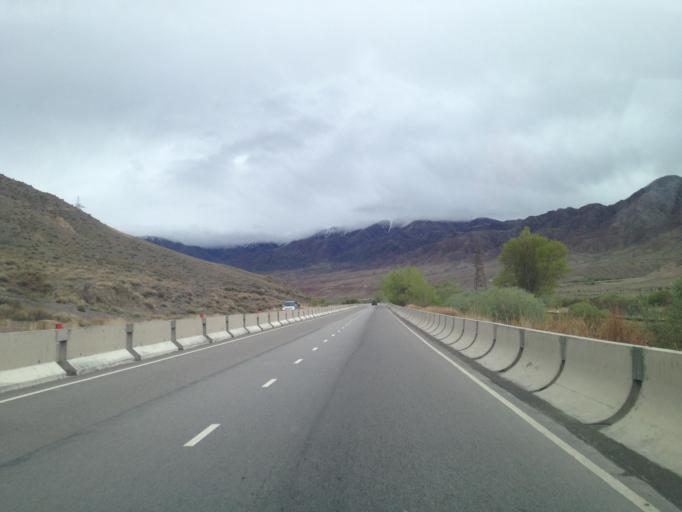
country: KG
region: Naryn
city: Kochkor
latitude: 42.4819
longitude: 75.8677
